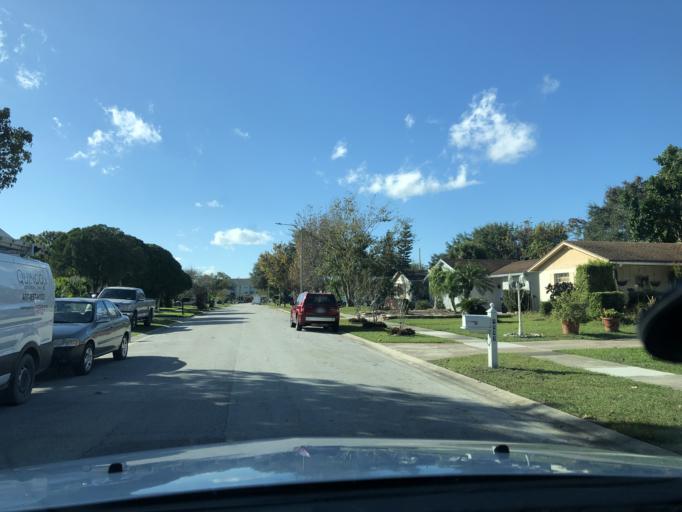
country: US
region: Florida
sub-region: Orange County
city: Oak Ridge
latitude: 28.4790
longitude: -81.4351
